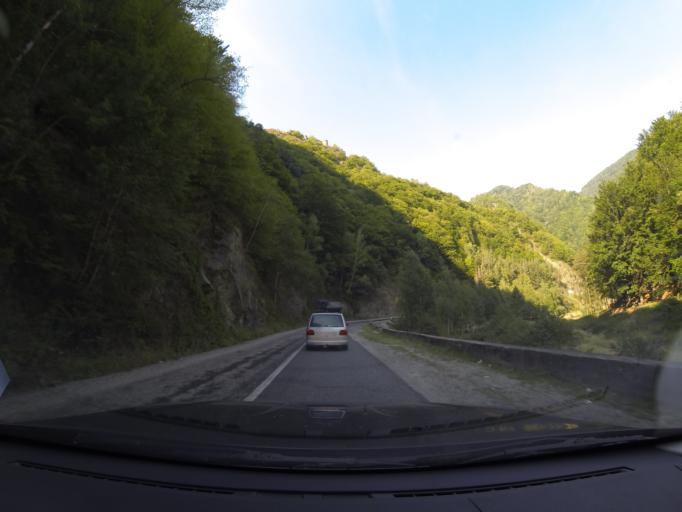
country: RO
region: Arges
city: Poenari
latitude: 45.3512
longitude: 24.6339
